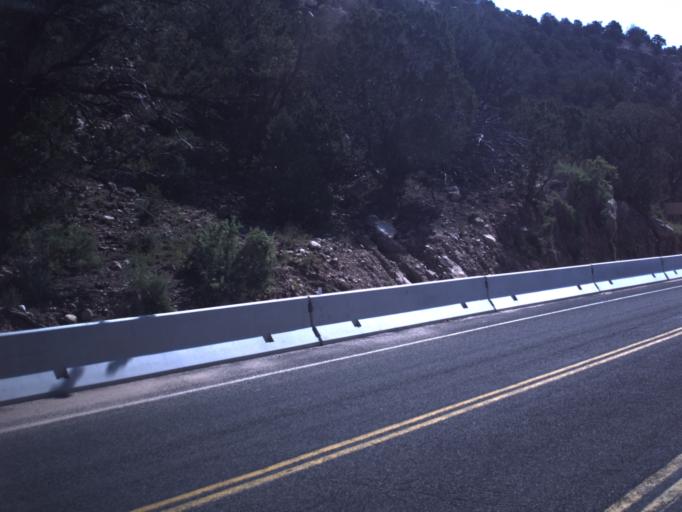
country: US
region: Utah
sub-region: Duchesne County
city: Duchesne
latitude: 40.3304
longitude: -110.6699
